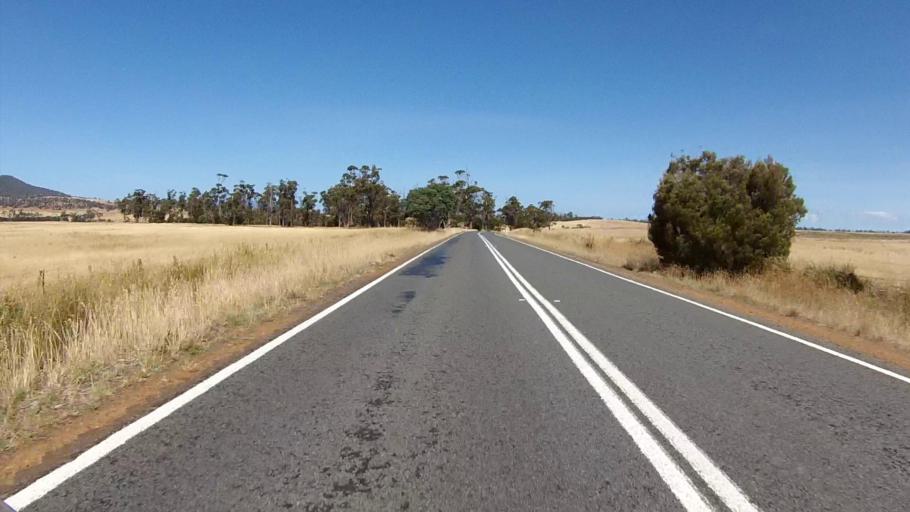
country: AU
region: Tasmania
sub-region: Sorell
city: Sorell
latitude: -42.4501
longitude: 147.9298
